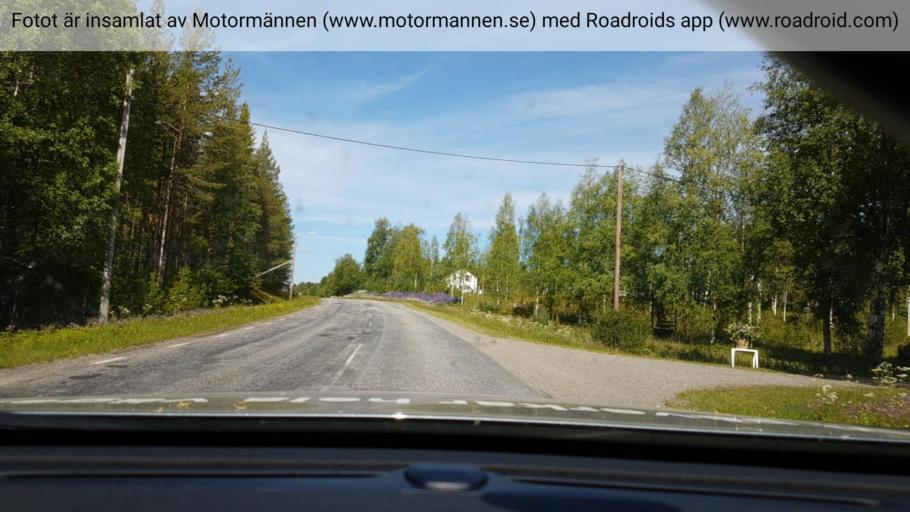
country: SE
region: Vaesterbotten
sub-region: Dorotea Kommun
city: Dorotea
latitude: 64.4081
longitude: 16.0497
